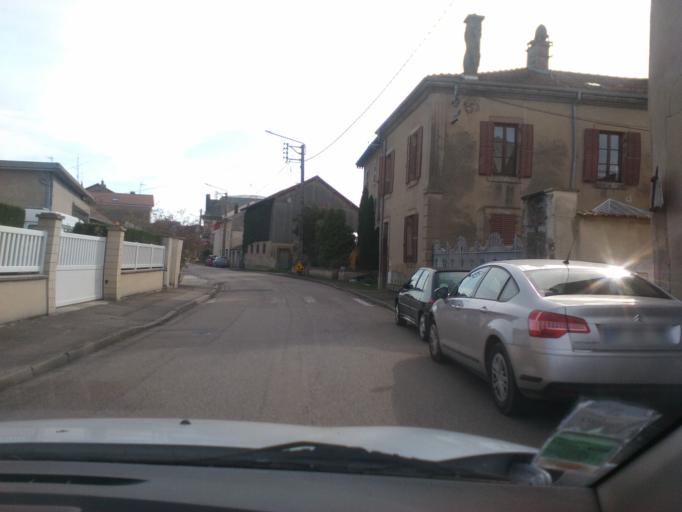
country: FR
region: Lorraine
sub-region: Departement des Vosges
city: Rambervillers
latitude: 48.3432
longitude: 6.6316
